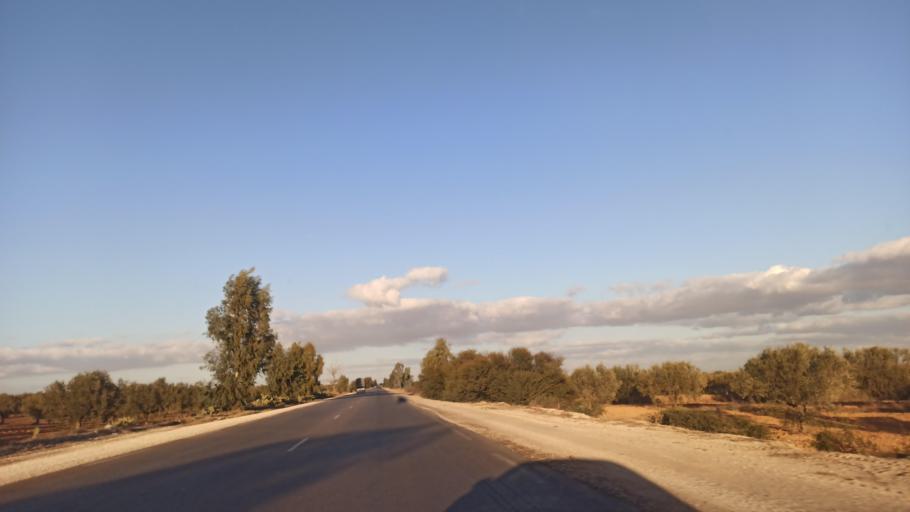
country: TN
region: Al Qayrawan
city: Sbikha
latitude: 35.8639
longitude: 10.2096
